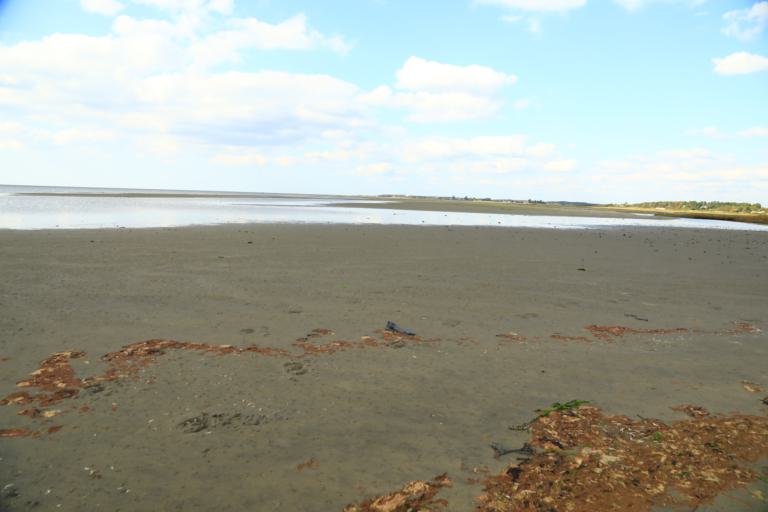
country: SE
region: Halland
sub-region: Varbergs Kommun
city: Tvaaker
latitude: 57.0097
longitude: 12.3437
